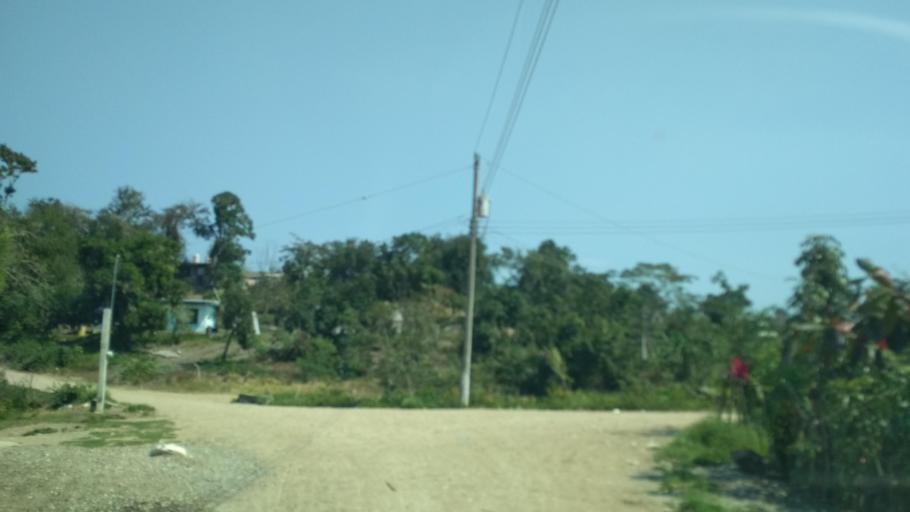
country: MX
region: Veracruz
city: Gutierrez Zamora
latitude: 20.4238
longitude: -97.1932
